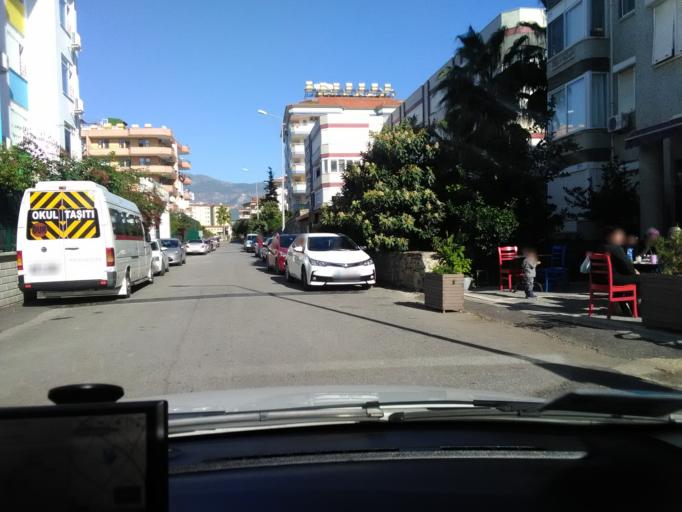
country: TR
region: Antalya
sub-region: Alanya
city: Alanya
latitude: 36.5361
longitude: 32.0415
